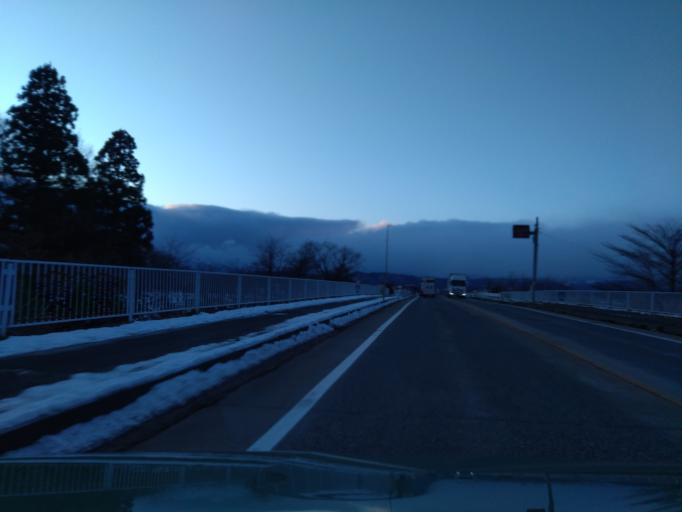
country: JP
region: Iwate
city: Shizukuishi
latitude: 39.6906
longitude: 140.9880
